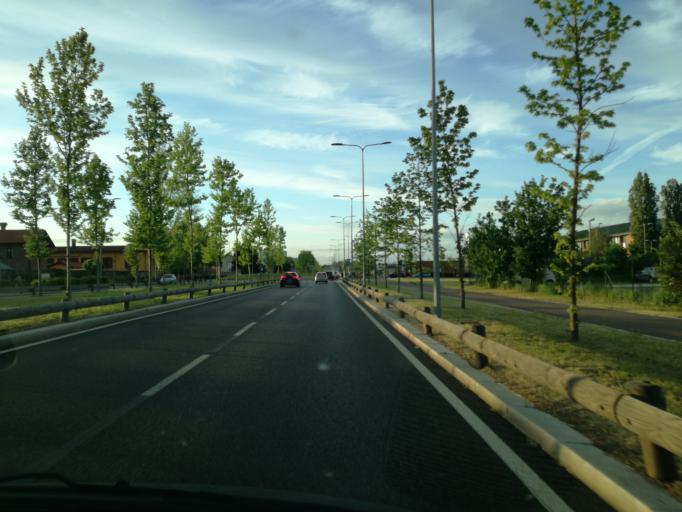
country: IT
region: Lombardy
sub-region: Citta metropolitana di Milano
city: Noverasco-Sporting Mirasole
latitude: 45.4124
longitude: 9.2068
